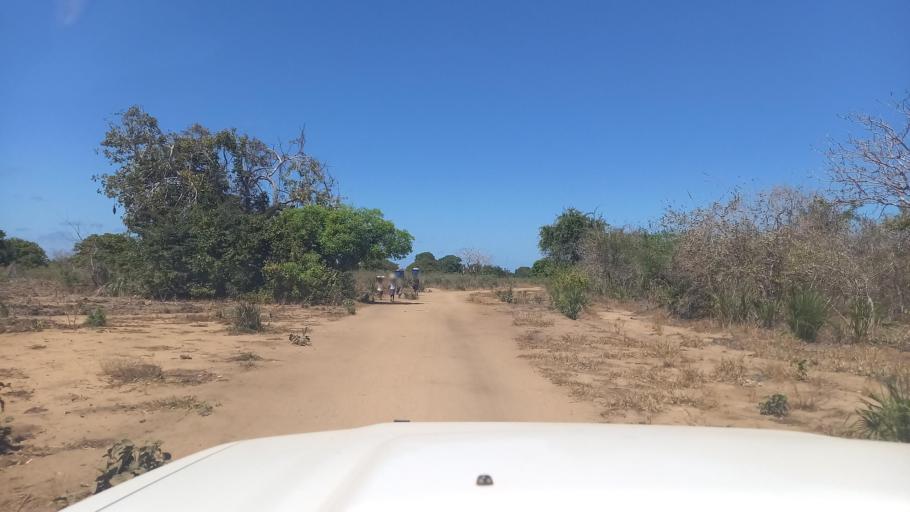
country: MZ
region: Cabo Delgado
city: Pemba
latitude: -13.4220
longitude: 40.5123
